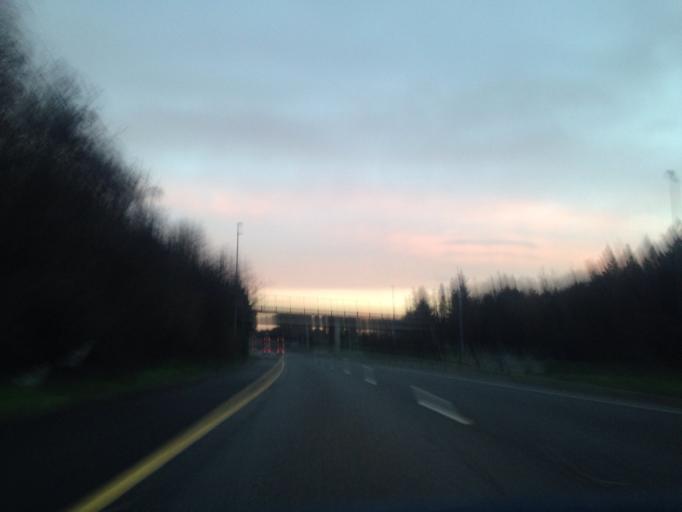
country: IE
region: Leinster
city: Little Bray
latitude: 53.1951
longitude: -6.1346
